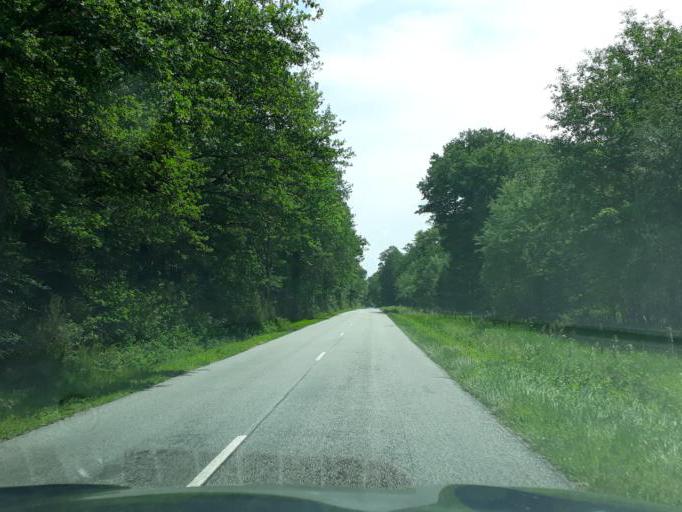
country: FR
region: Centre
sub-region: Departement du Loiret
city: Vienne-en-Val
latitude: 47.7452
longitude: 2.1513
